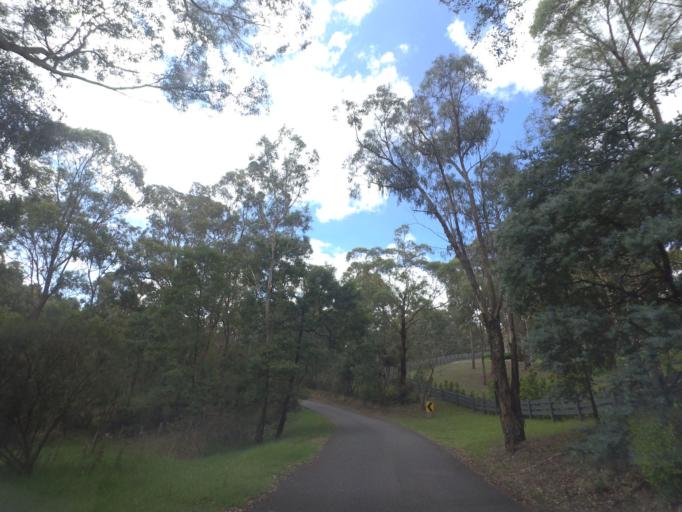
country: AU
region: Victoria
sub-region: Manningham
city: Park Orchards
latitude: -37.7760
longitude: 145.1988
